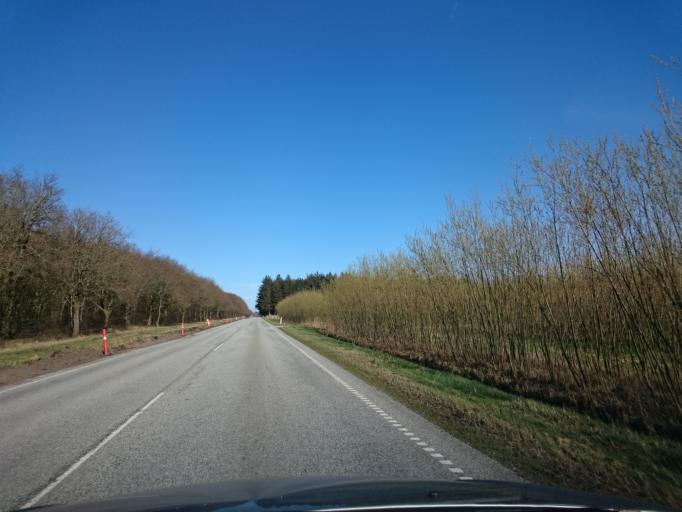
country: DK
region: North Denmark
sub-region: Hjorring Kommune
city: Sindal
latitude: 57.5876
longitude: 10.2520
